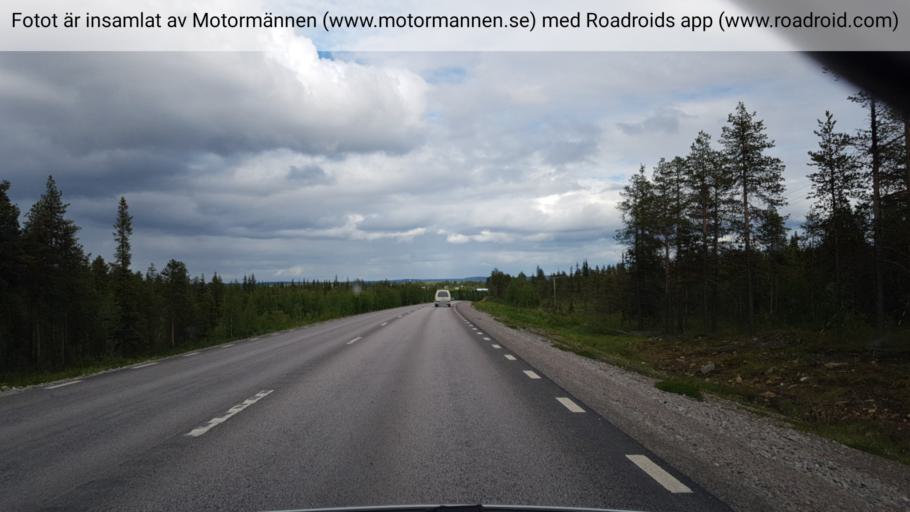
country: SE
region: Norrbotten
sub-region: Gallivare Kommun
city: Malmberget
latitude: 67.6688
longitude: 21.6091
